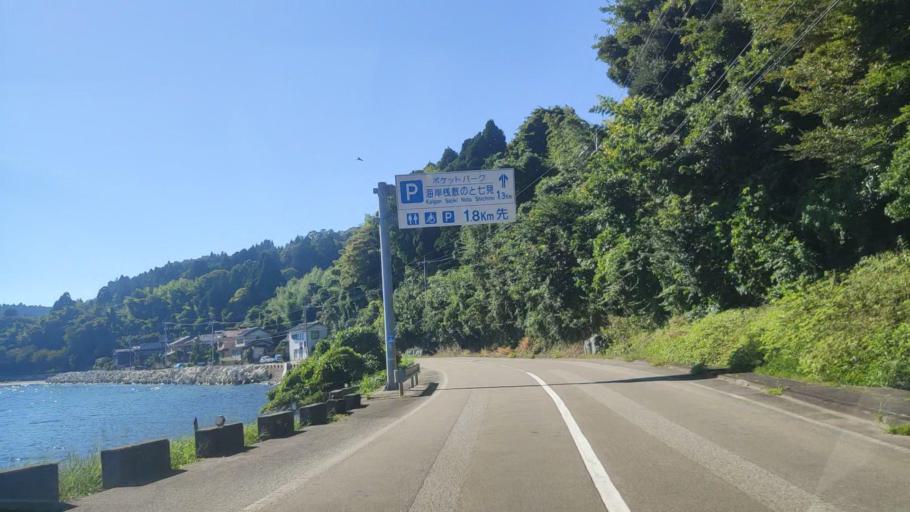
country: JP
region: Ishikawa
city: Nanao
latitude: 37.2796
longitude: 137.1023
